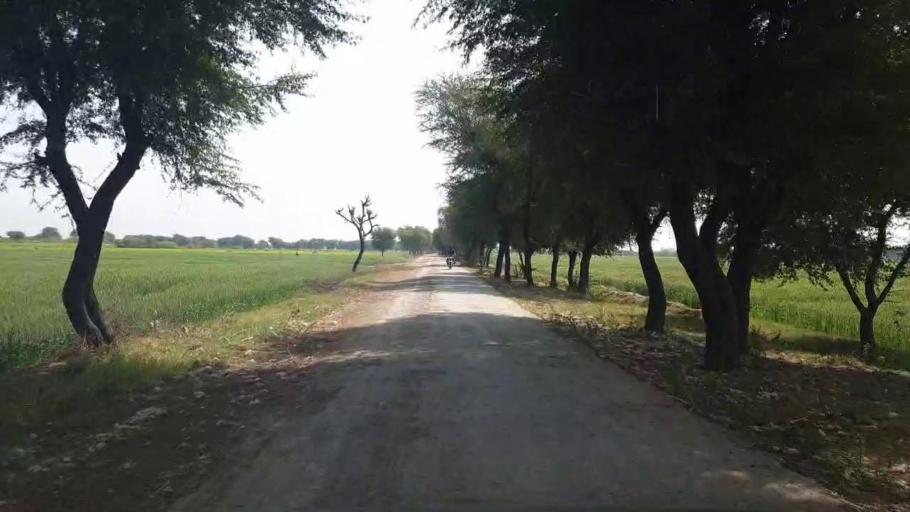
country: PK
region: Sindh
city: Umarkot
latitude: 25.3336
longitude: 69.6093
